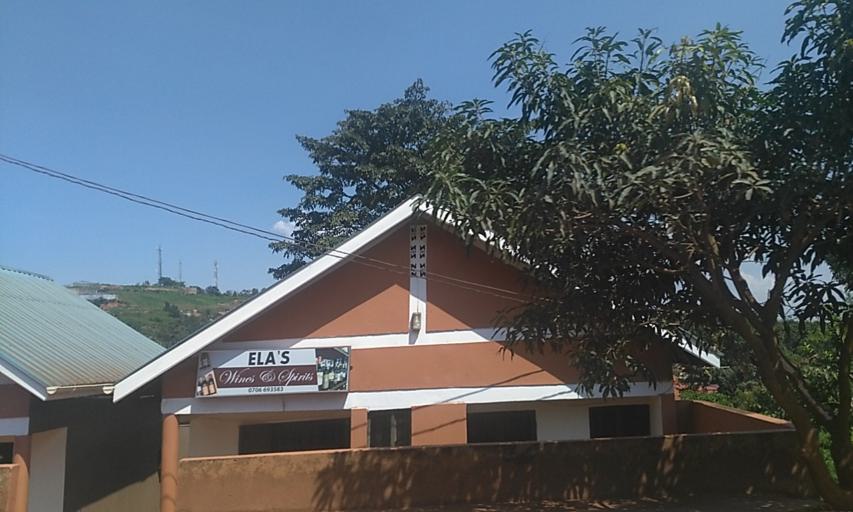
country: UG
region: Central Region
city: Kampala Central Division
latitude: 0.3871
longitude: 32.5931
